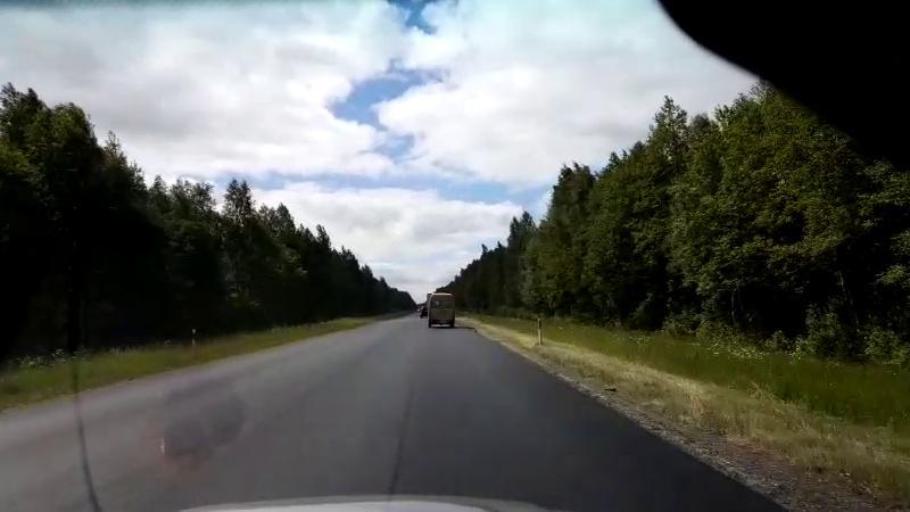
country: LV
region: Salacgrivas
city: Ainazi
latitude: 57.9603
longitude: 24.4432
